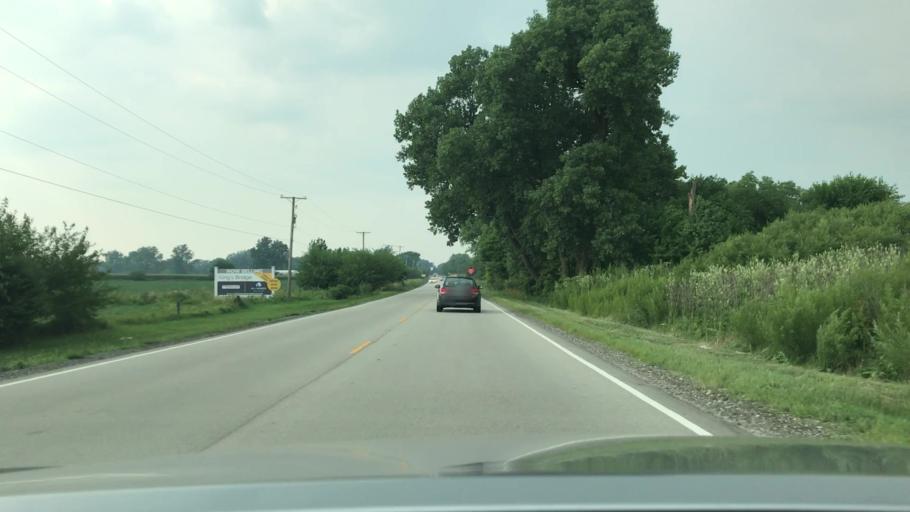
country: US
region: Illinois
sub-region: Will County
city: Plainfield
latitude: 41.6586
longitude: -88.2355
